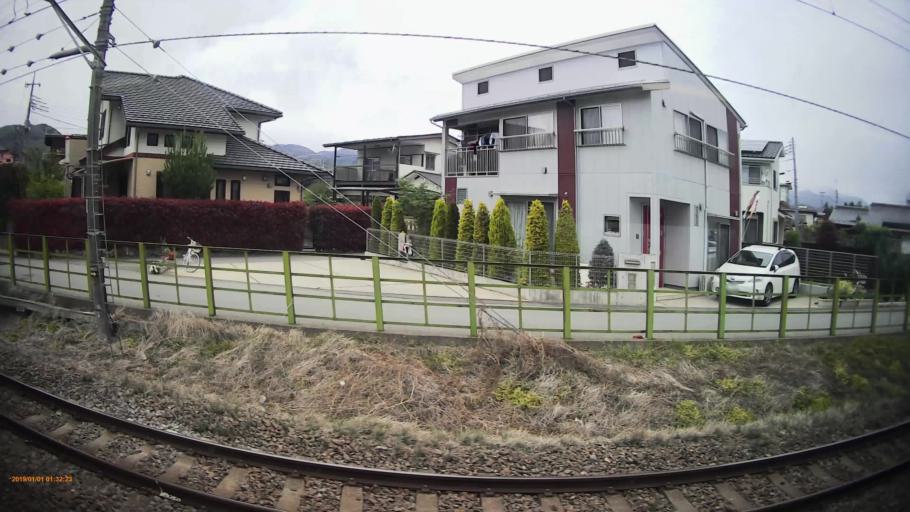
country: JP
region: Yamanashi
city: Enzan
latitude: 35.6858
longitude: 138.6877
